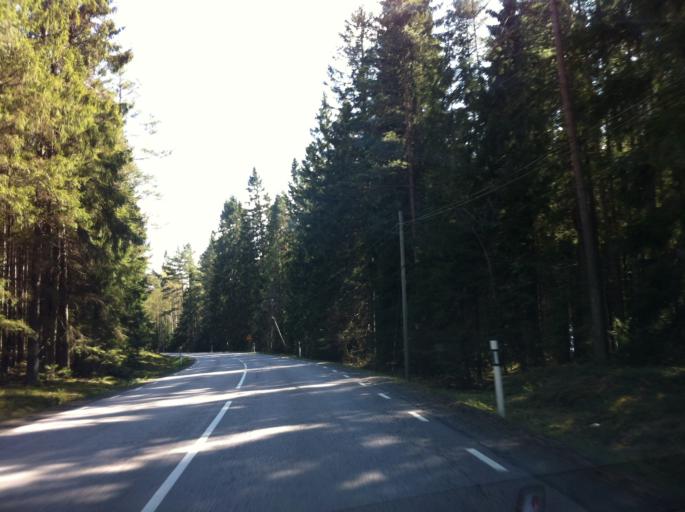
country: SE
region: Vaestra Goetaland
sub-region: Alingsas Kommun
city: Alingsas
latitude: 57.8554
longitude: 12.6175
